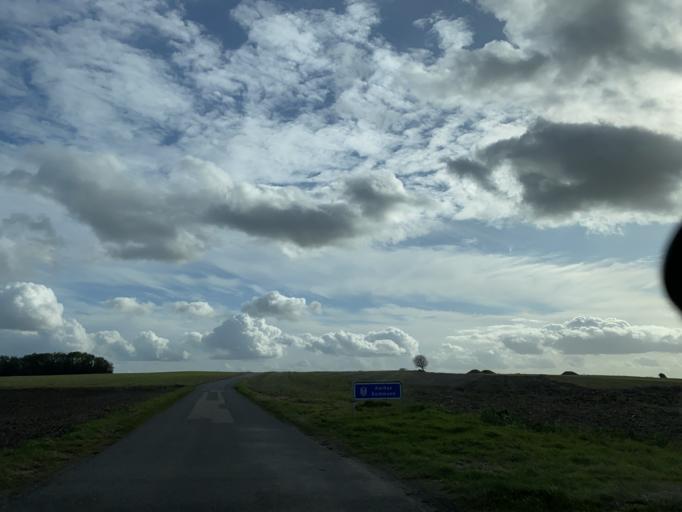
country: DK
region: Central Jutland
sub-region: Arhus Kommune
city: Sabro
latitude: 56.2060
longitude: 9.9907
